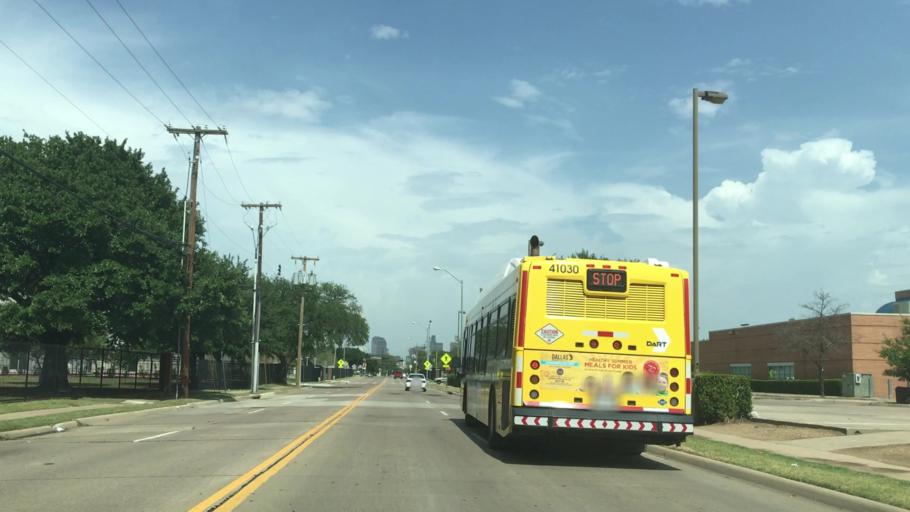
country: US
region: Texas
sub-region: Dallas County
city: Dallas
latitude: 32.7872
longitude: -96.8597
